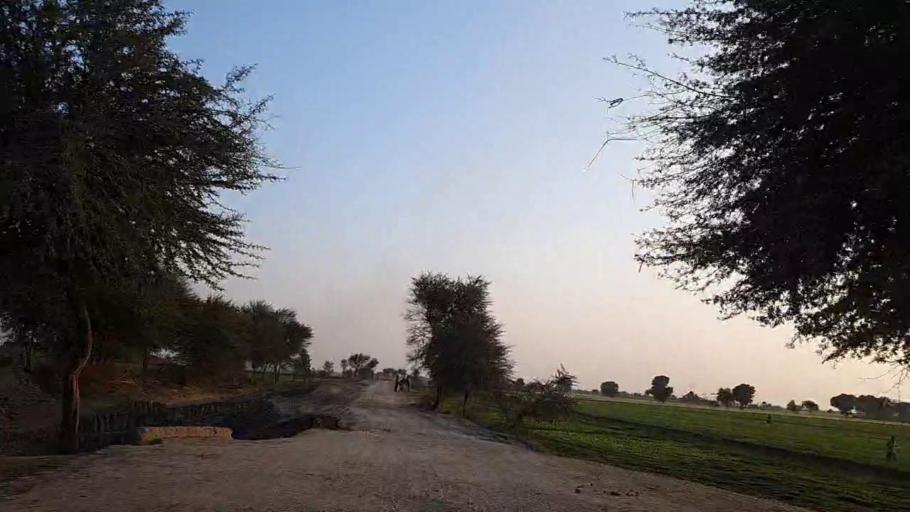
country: PK
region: Sindh
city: Shahdadpur
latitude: 25.9561
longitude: 68.5009
